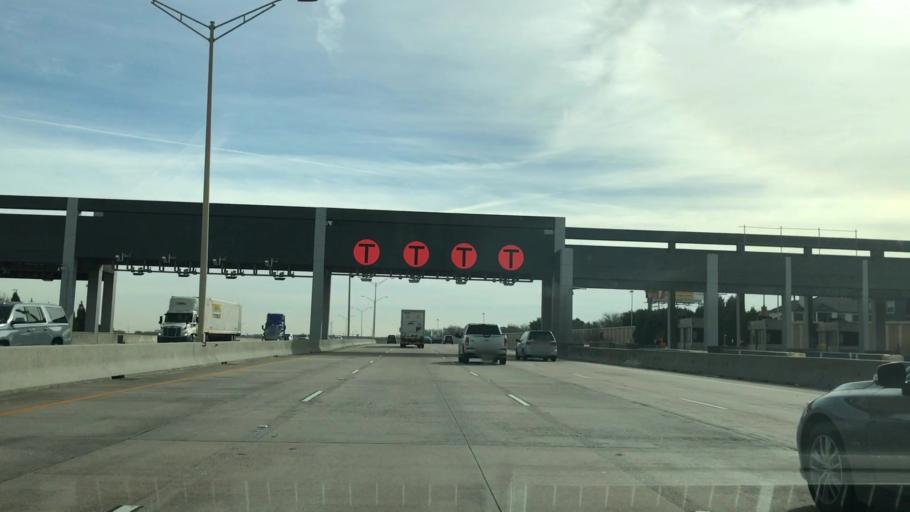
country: US
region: Texas
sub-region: Dallas County
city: Addison
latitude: 33.0027
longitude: -96.7769
